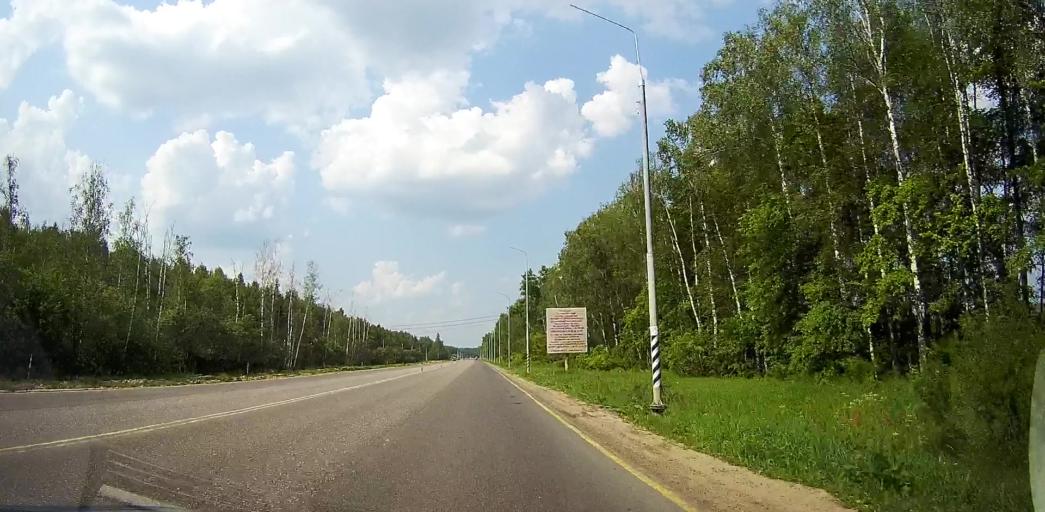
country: RU
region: Moskovskaya
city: Mikhnevo
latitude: 55.0643
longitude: 37.9537
